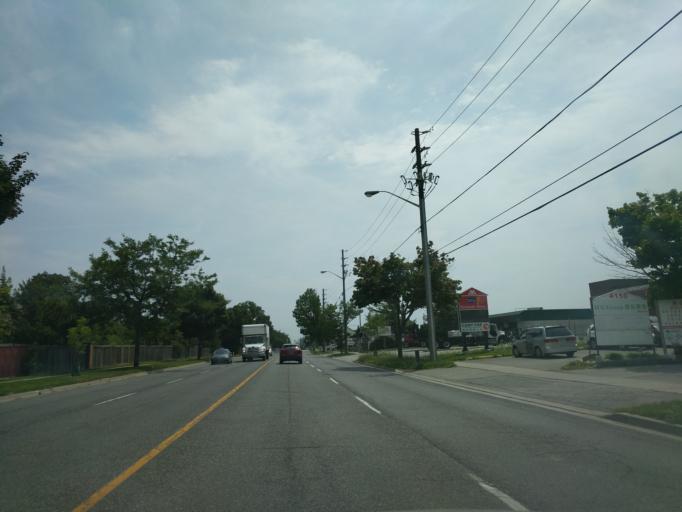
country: CA
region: Ontario
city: Markham
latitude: 43.8232
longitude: -79.2960
